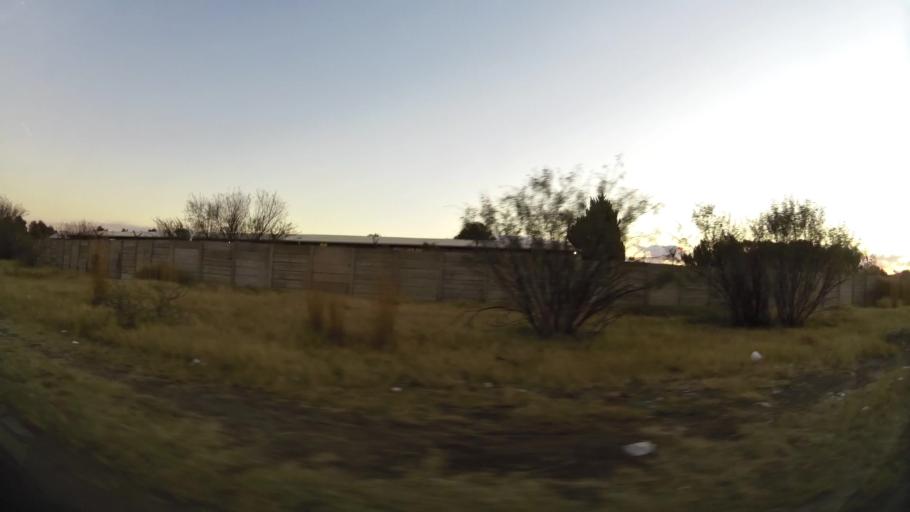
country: ZA
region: Northern Cape
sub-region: Frances Baard District Municipality
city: Kimberley
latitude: -28.7127
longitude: 24.7722
